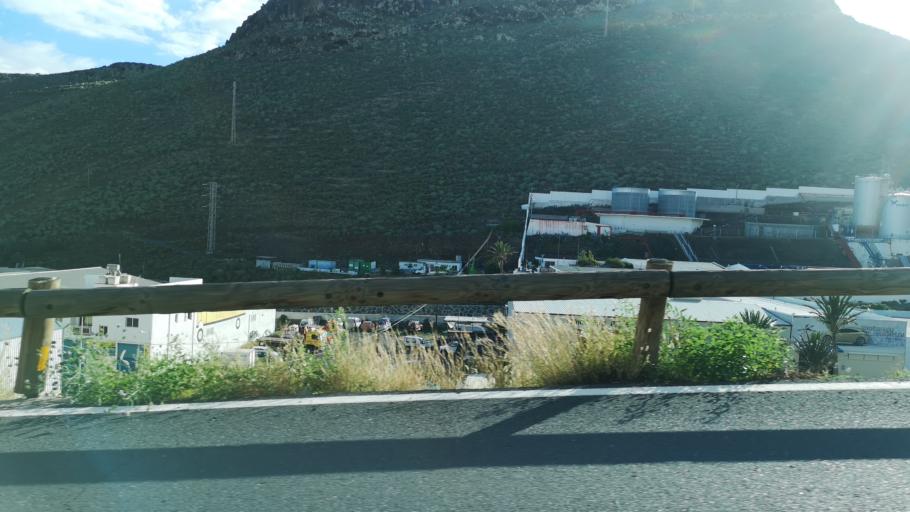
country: ES
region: Canary Islands
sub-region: Provincia de Santa Cruz de Tenerife
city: San Sebastian de la Gomera
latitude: 28.0895
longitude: -17.1167
